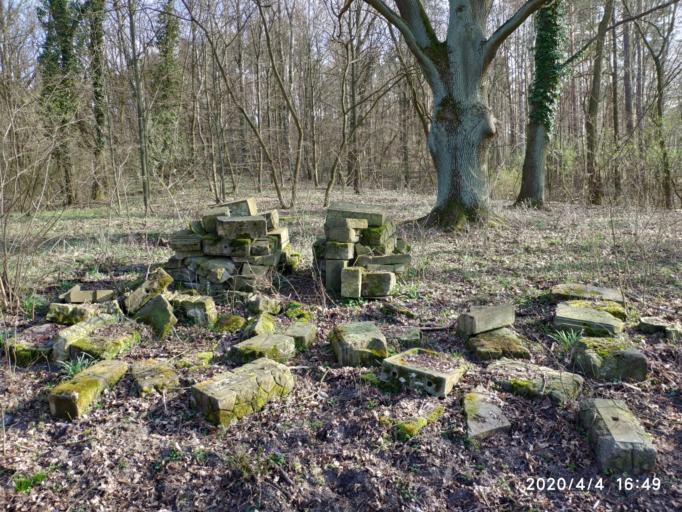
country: PL
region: Lubusz
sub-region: Powiat zielonogorski
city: Swidnica
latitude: 51.8941
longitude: 15.2836
